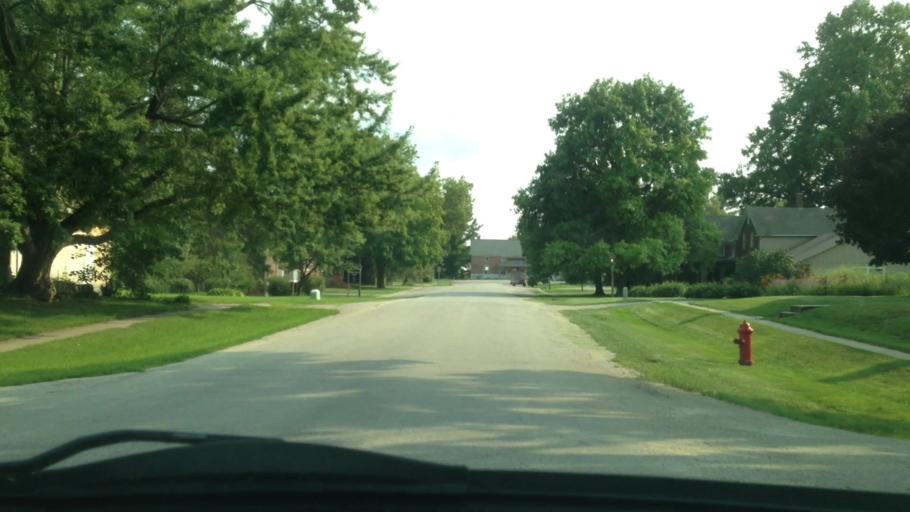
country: US
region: Iowa
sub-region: Benton County
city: Walford
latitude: 41.7959
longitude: -91.9025
